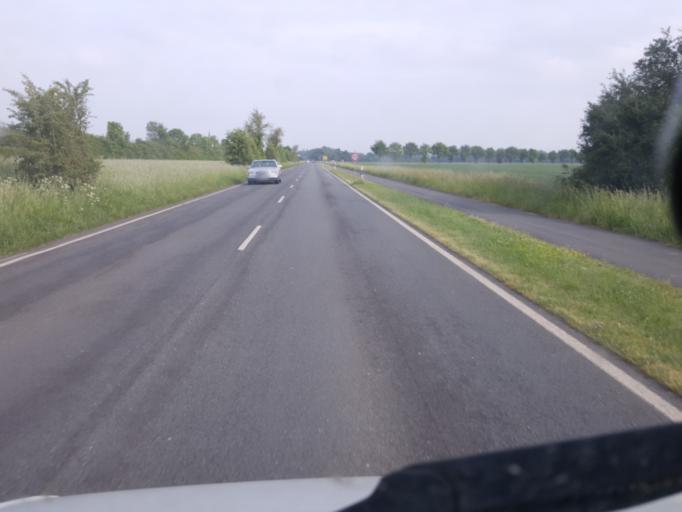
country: DE
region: Lower Saxony
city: Marklohe
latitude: 52.6511
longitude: 9.1905
